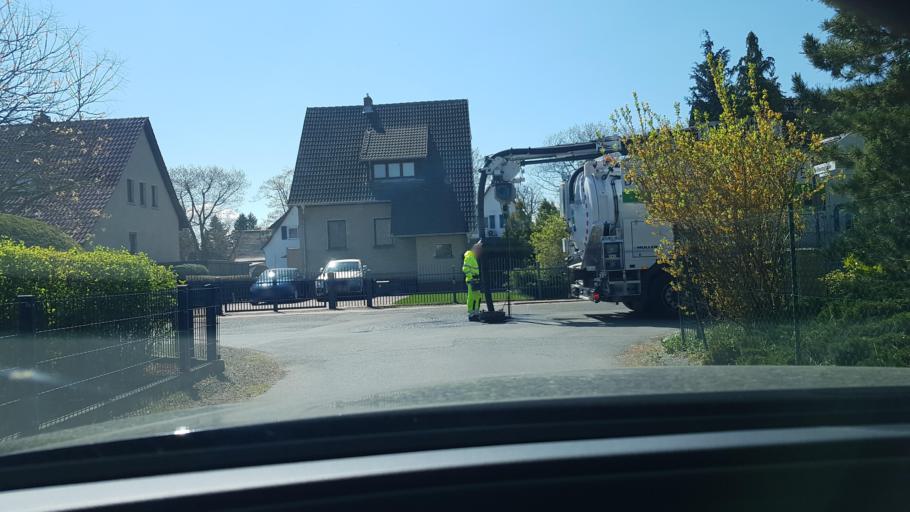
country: DE
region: Brandenburg
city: Rangsdorf
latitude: 52.3378
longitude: 13.4043
